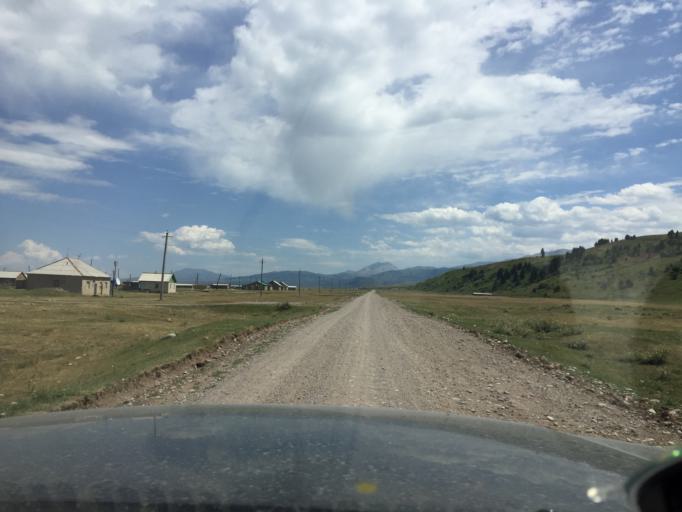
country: KZ
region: Almaty Oblysy
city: Kegen
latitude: 42.7589
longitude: 79.1478
